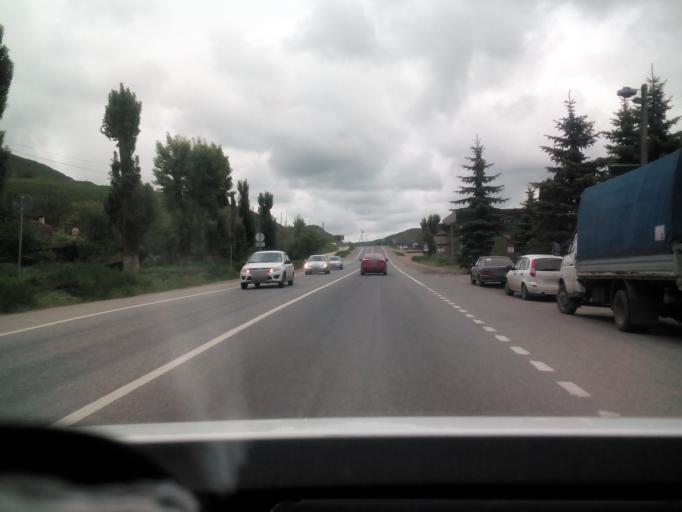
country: RU
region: Stavropol'skiy
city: Yasnaya Polyana
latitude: 43.9714
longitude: 42.7833
